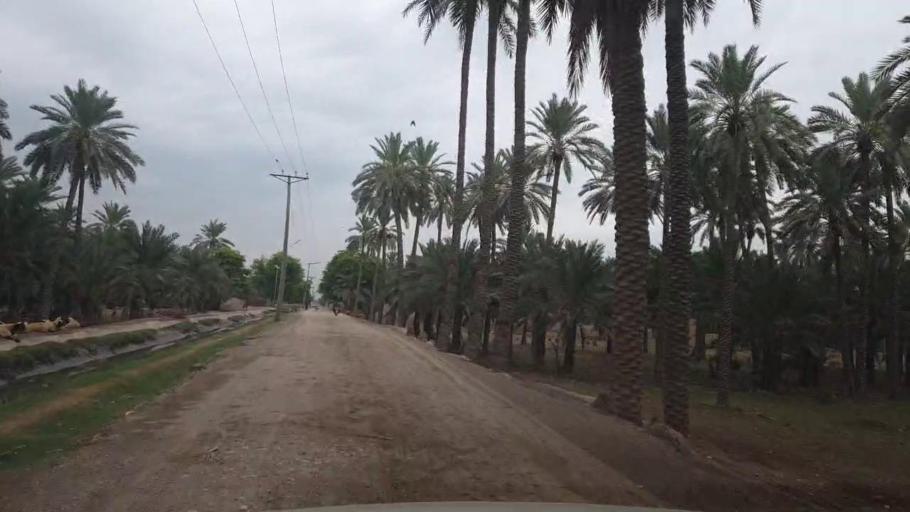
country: PK
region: Sindh
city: Sukkur
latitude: 27.6181
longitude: 68.8188
